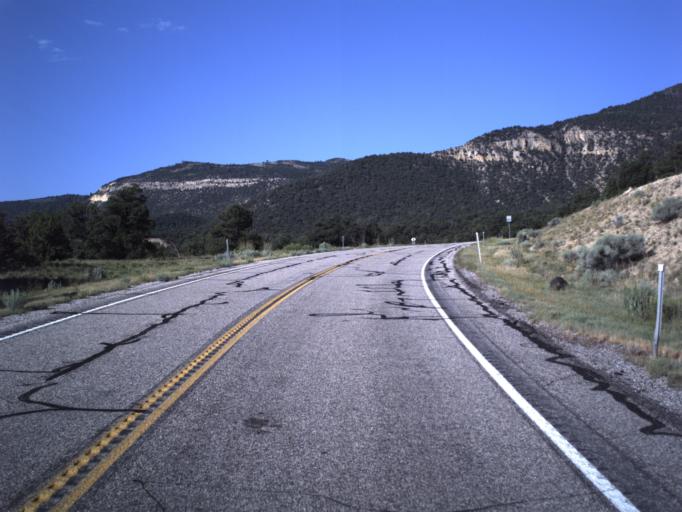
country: US
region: Utah
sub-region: Wayne County
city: Loa
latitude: 38.7329
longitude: -111.3954
